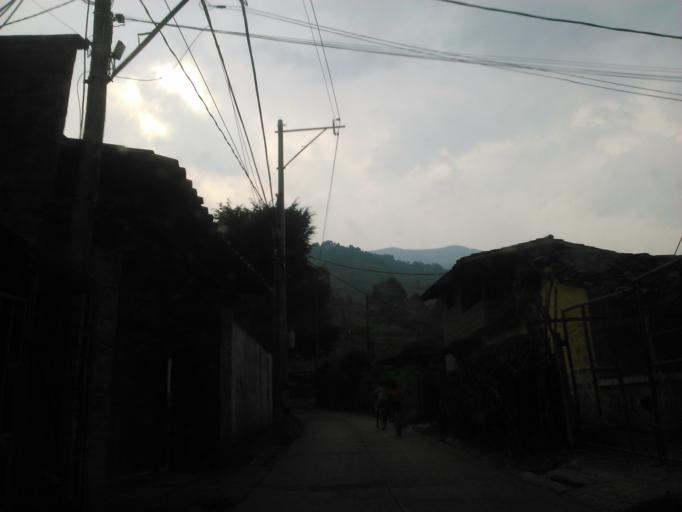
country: CO
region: Antioquia
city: La Estrella
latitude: 6.1380
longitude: -75.6430
